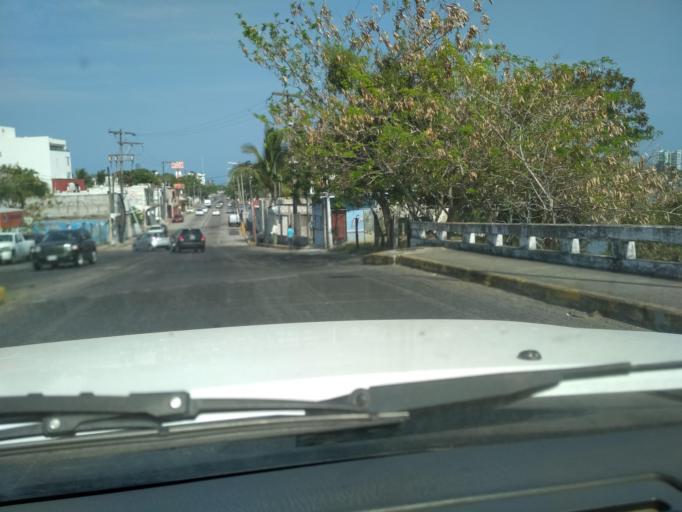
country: MX
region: Veracruz
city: Boca del Rio
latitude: 19.0998
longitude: -96.1114
